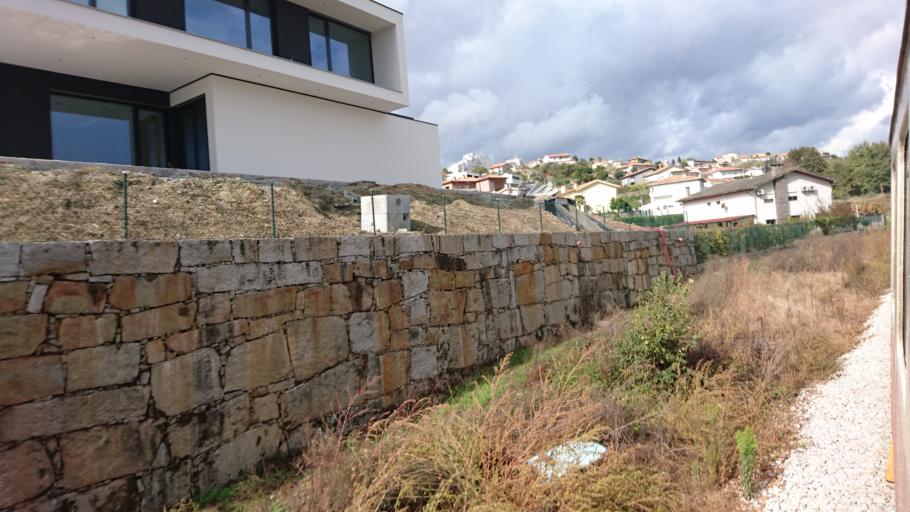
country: PT
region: Porto
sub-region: Marco de Canaveses
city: Marco de Canavezes
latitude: 41.1856
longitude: -8.1401
